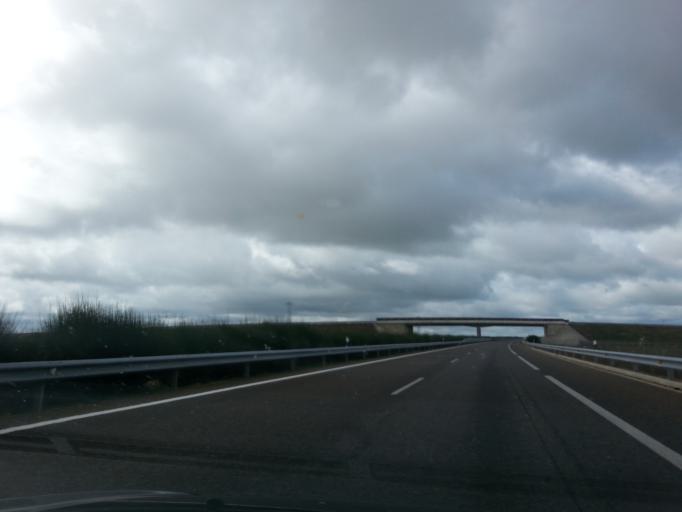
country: ES
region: Castille and Leon
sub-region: Provincia de Salamanca
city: La Fuente de San Esteban
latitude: 40.7969
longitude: -6.2106
